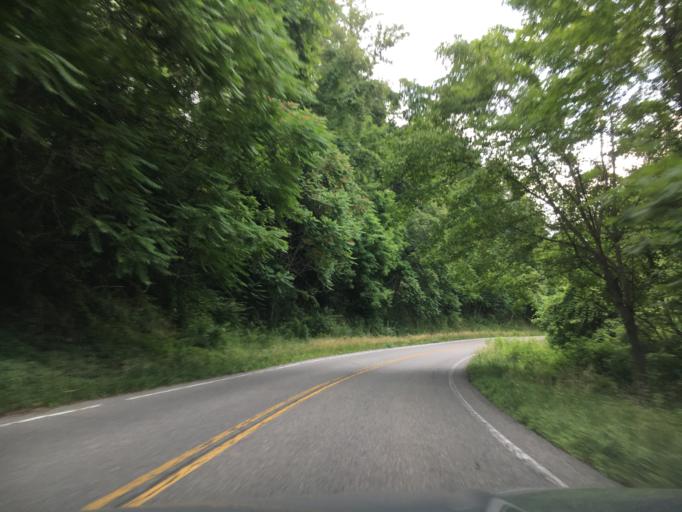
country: US
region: Virginia
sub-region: Roanoke County
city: Narrows
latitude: 37.1753
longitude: -80.0020
